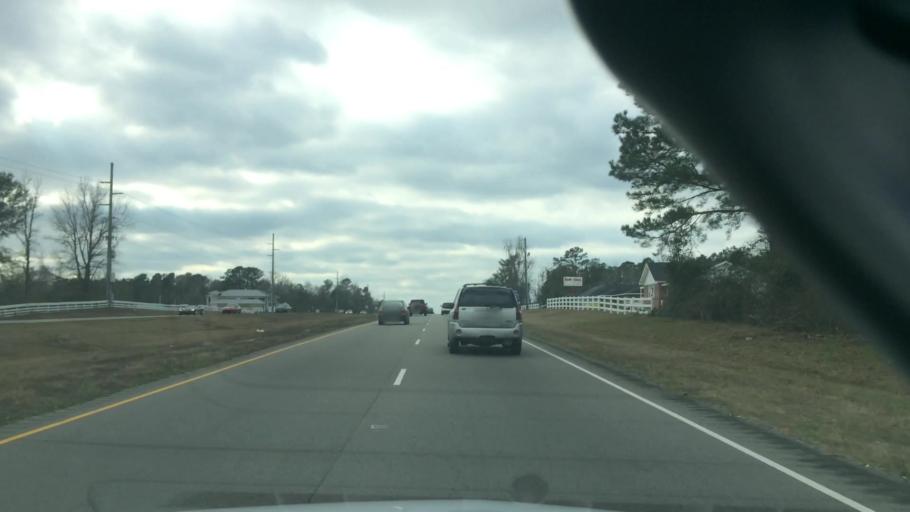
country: US
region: North Carolina
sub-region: Brunswick County
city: Shallotte
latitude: 34.0119
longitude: -78.2896
